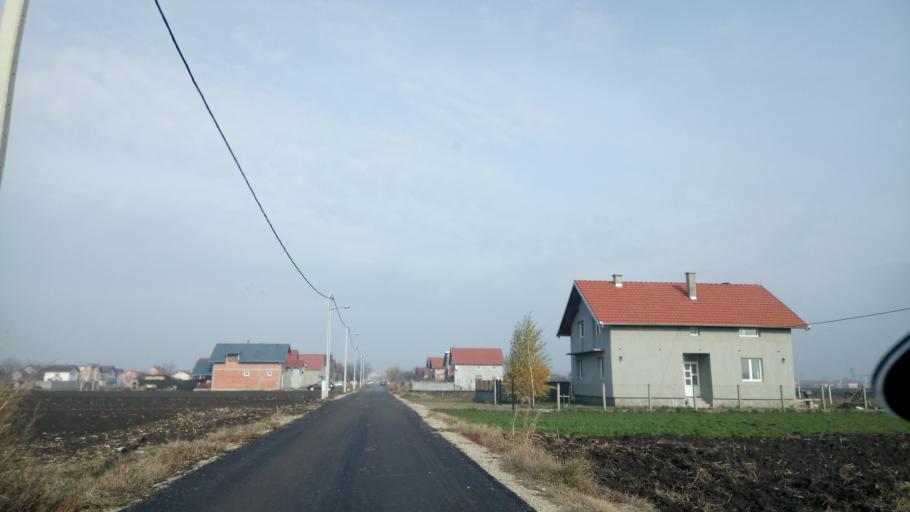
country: RS
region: Autonomna Pokrajina Vojvodina
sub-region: Sremski Okrug
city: Stara Pazova
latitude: 44.9780
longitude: 20.1736
